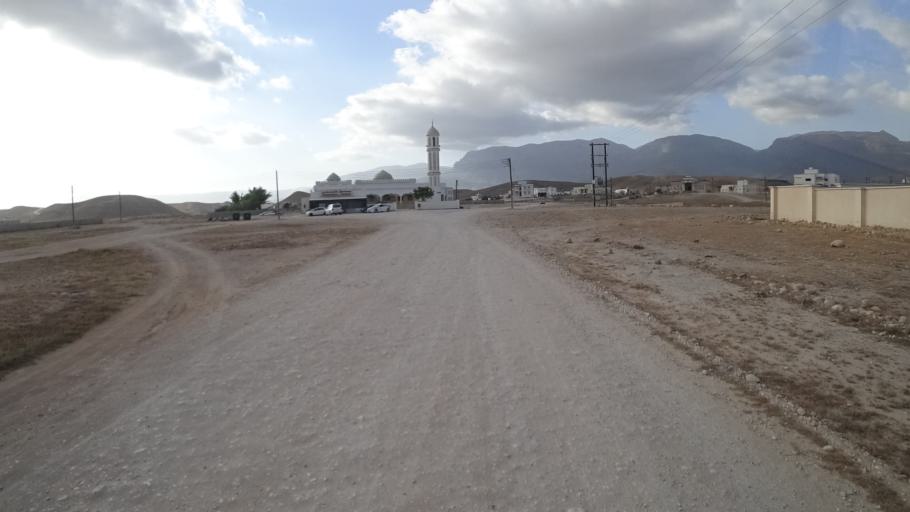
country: OM
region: Zufar
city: Salalah
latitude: 16.9603
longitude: 53.8672
